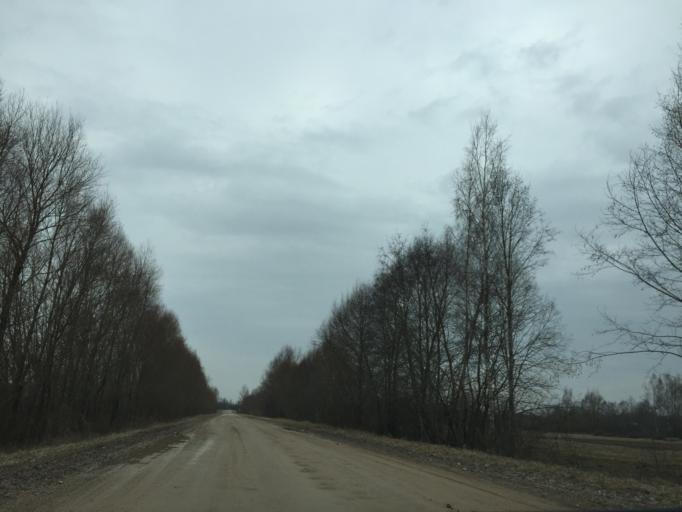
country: LV
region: Jelgava
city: Jelgava
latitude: 56.6965
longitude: 23.7240
